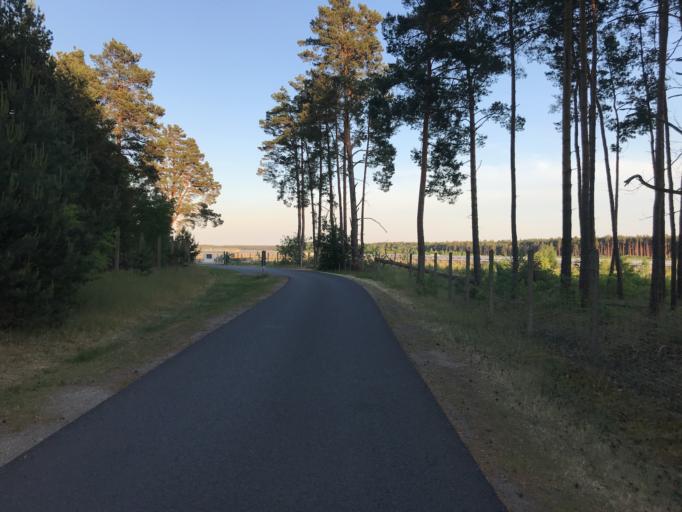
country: DE
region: Brandenburg
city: Melchow
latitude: 52.8317
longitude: 13.6743
